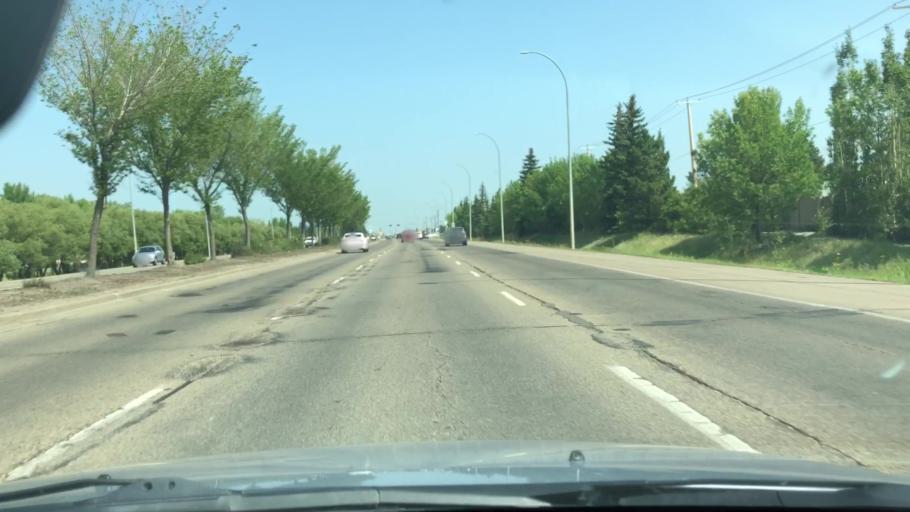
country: CA
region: Alberta
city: Edmonton
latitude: 53.6107
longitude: -113.4917
